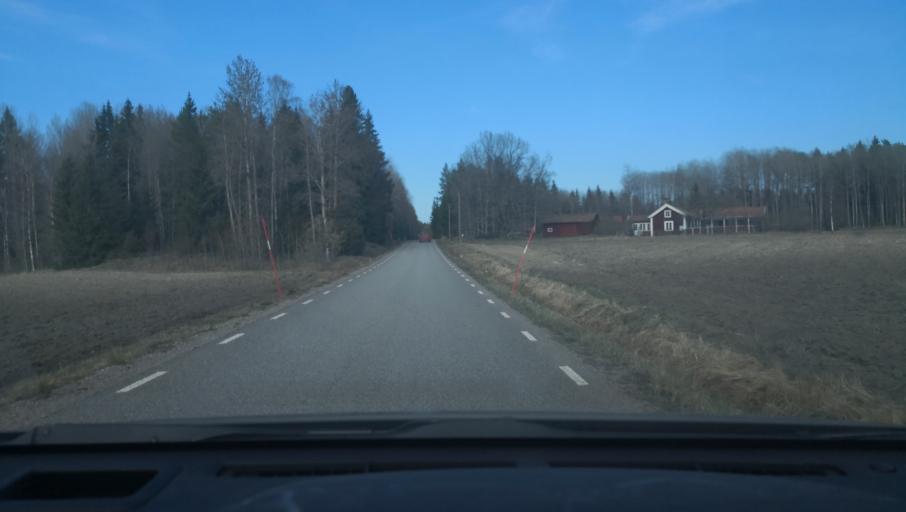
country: SE
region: Uppsala
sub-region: Heby Kommun
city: Heby
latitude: 59.9028
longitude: 16.8115
